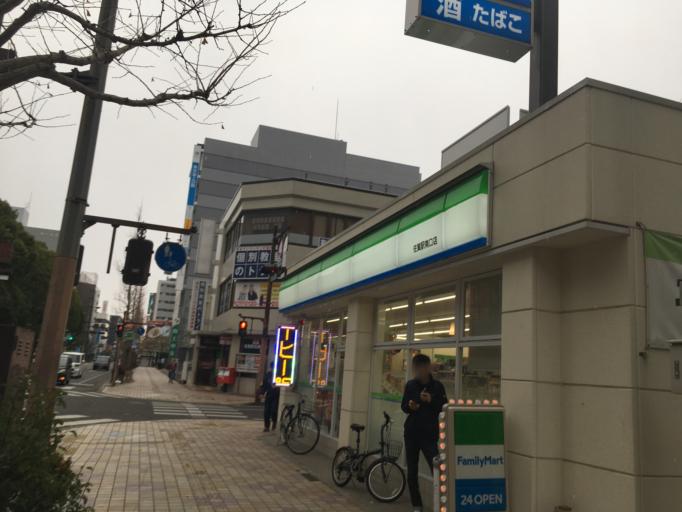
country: JP
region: Saga Prefecture
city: Saga-shi
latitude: 33.2631
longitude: 130.2979
